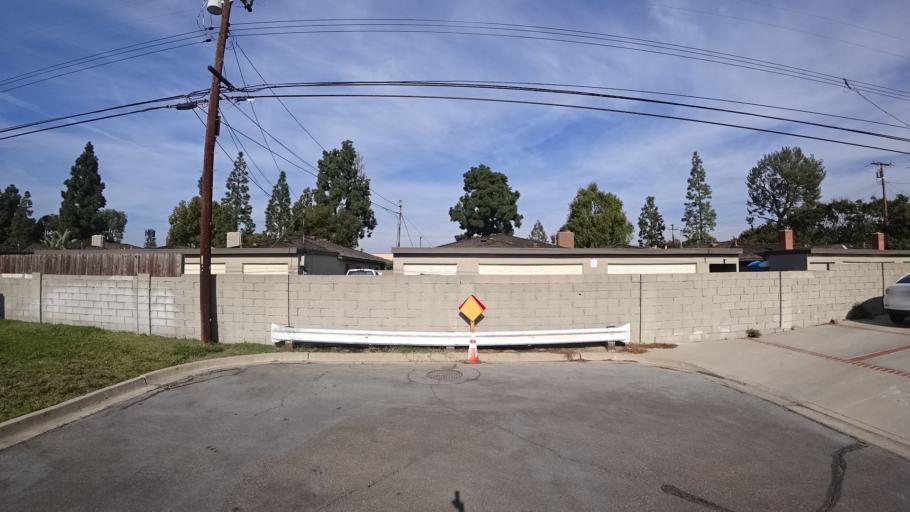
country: US
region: California
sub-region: Orange County
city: Garden Grove
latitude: 33.8004
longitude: -117.9375
